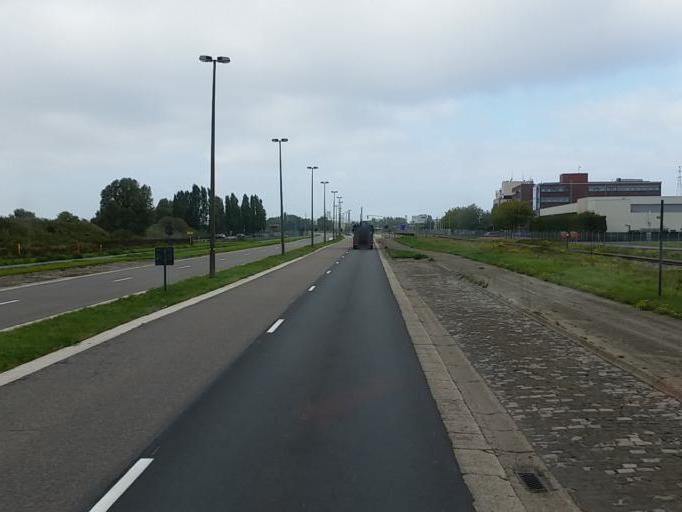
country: BE
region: Flanders
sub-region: Provincie Antwerpen
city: Stabroek
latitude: 51.2908
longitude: 4.3231
